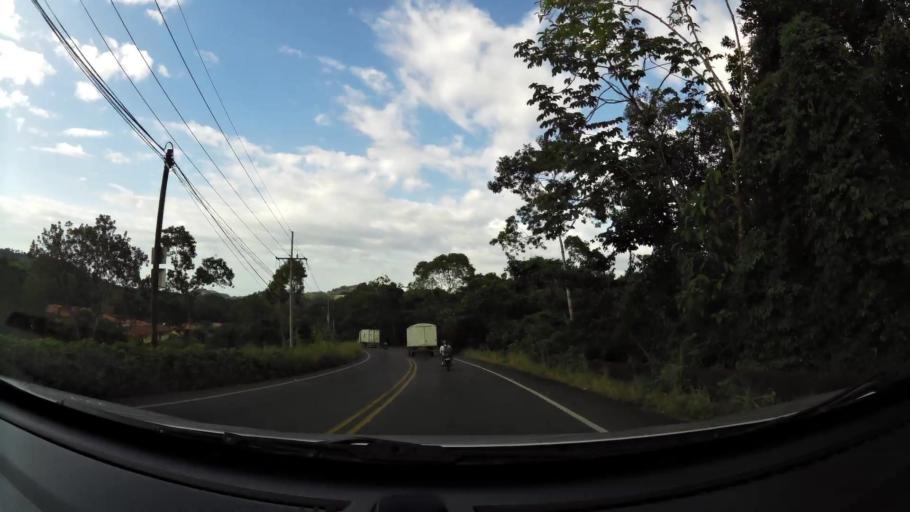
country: CR
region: Puntarenas
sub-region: Canton de Garabito
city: Jaco
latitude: 9.7055
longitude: -84.6346
